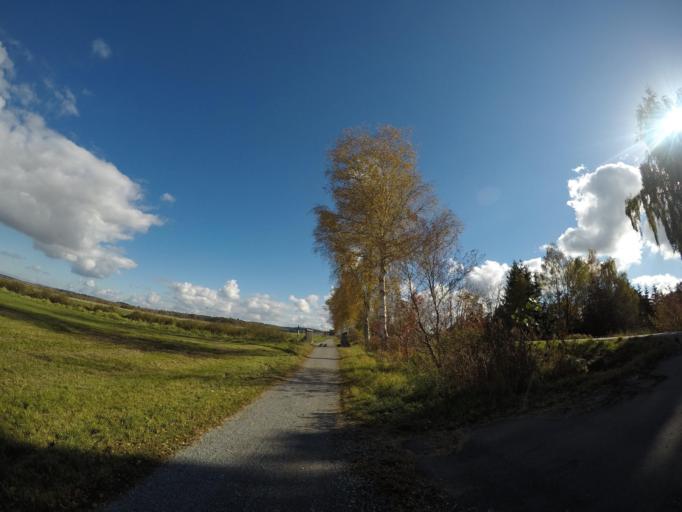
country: DE
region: Baden-Wuerttemberg
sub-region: Tuebingen Region
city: Bad Buchau
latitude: 48.0662
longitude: 9.6181
